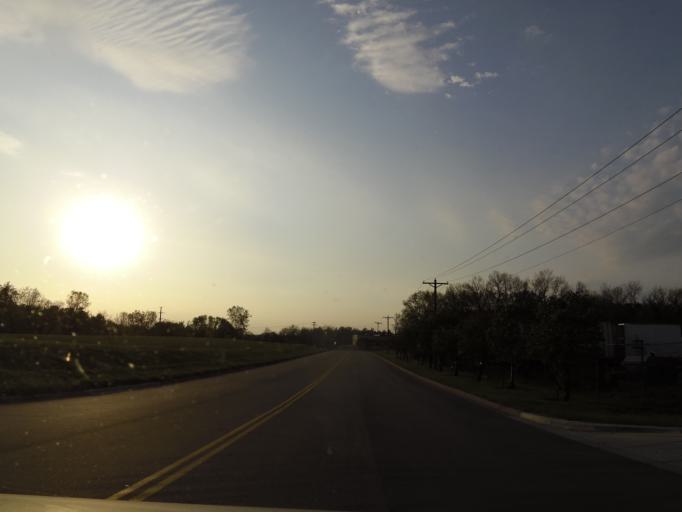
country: US
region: Minnesota
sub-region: Dakota County
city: Eagan
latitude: 44.8281
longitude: -93.2000
